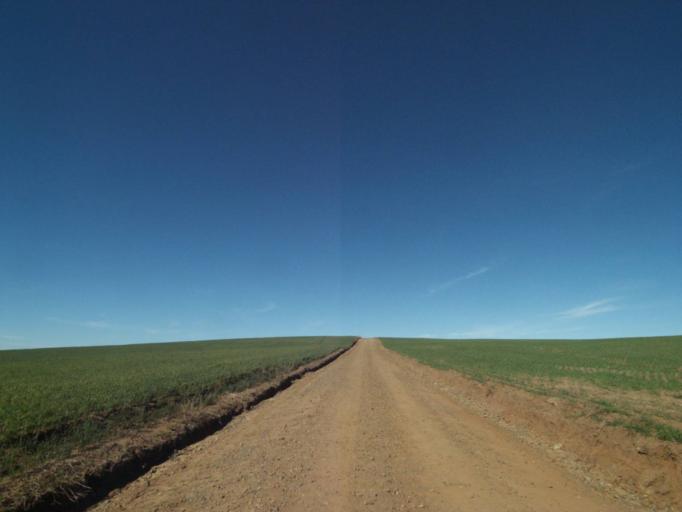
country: BR
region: Parana
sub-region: Tibagi
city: Tibagi
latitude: -24.5713
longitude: -50.2661
